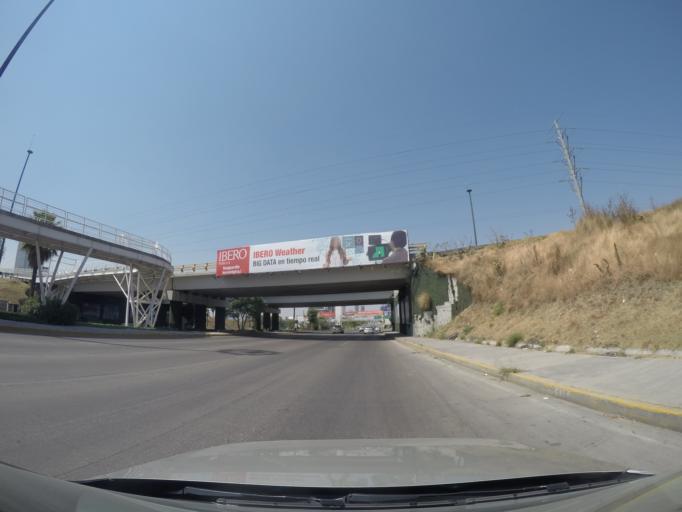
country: MX
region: Puebla
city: Tlazcalancingo
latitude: 19.0192
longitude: -98.2487
